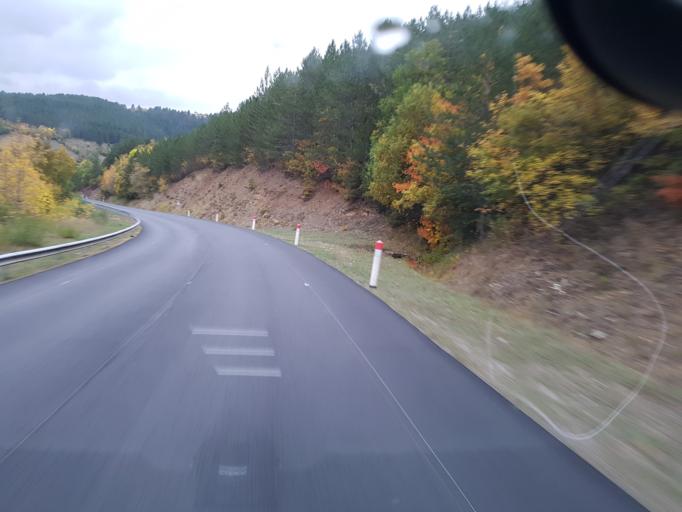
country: FR
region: Languedoc-Roussillon
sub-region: Departement de la Lozere
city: Mende
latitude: 44.5376
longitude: 3.5775
